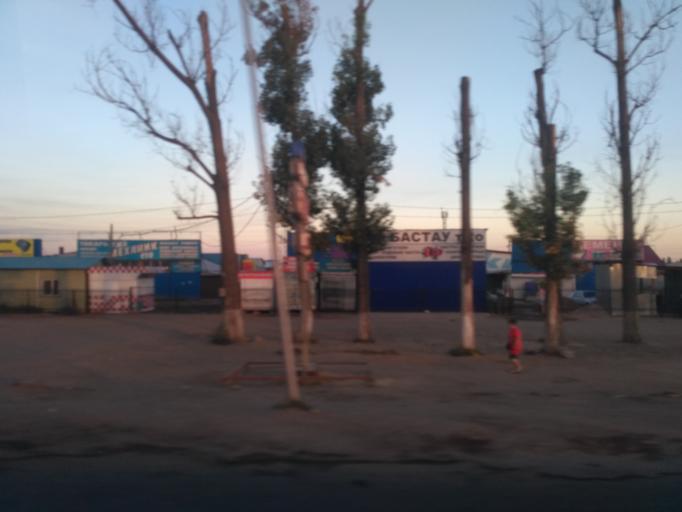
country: KZ
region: Almaty Oblysy
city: Pervomayskiy
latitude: 43.3247
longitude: 76.9071
